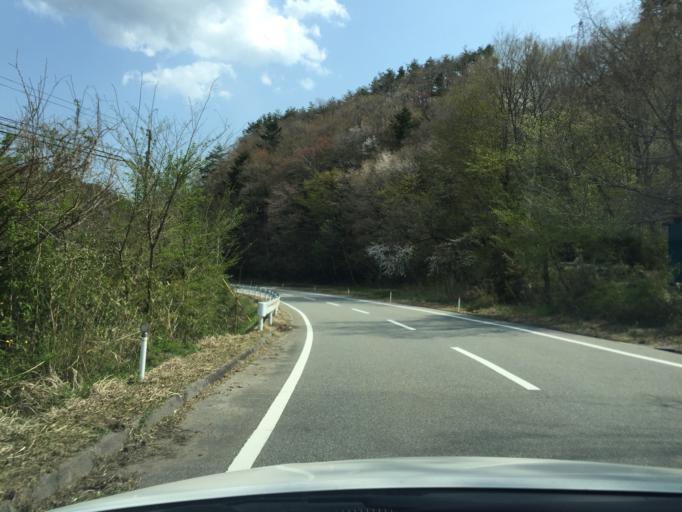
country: JP
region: Fukushima
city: Namie
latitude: 37.3068
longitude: 140.8347
